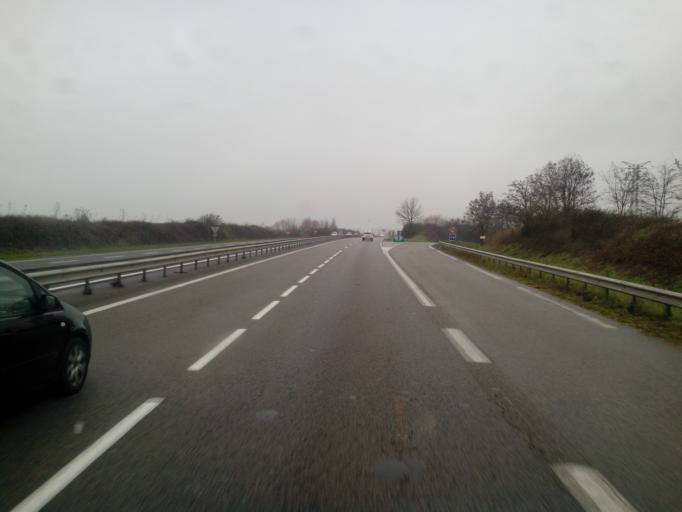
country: FR
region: Poitou-Charentes
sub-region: Departement de la Vienne
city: Mignaloux-Beauvoir
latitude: 46.5821
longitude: 0.3941
